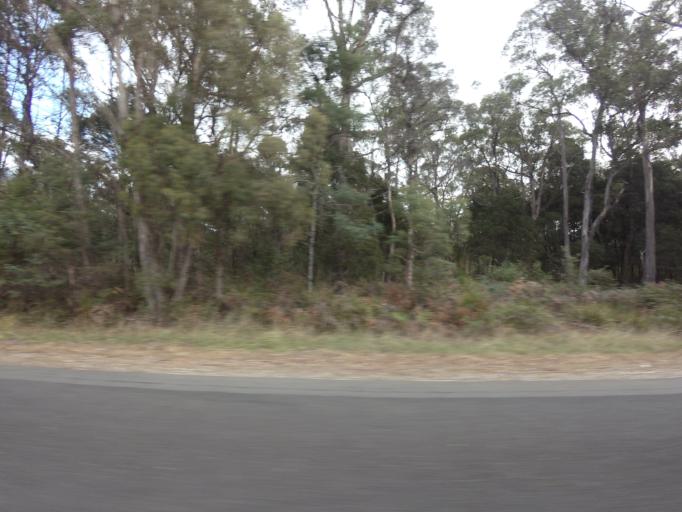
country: AU
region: Tasmania
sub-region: Meander Valley
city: Deloraine
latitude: -41.6165
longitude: 146.6921
